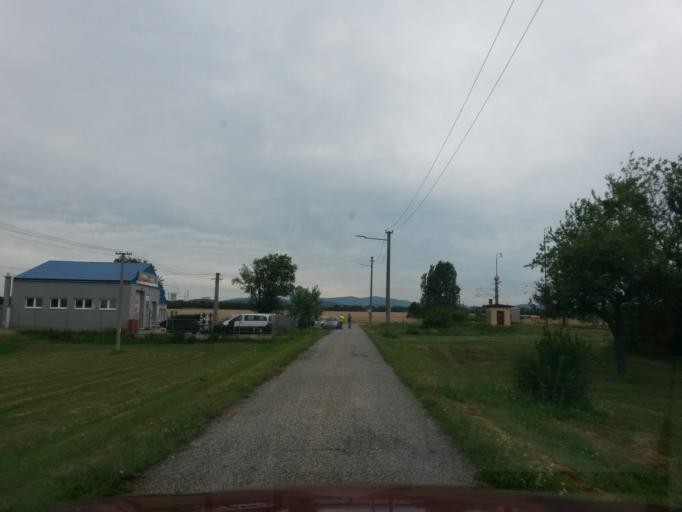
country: SK
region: Nitriansky
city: Tlmace
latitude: 48.1860
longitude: 18.4726
